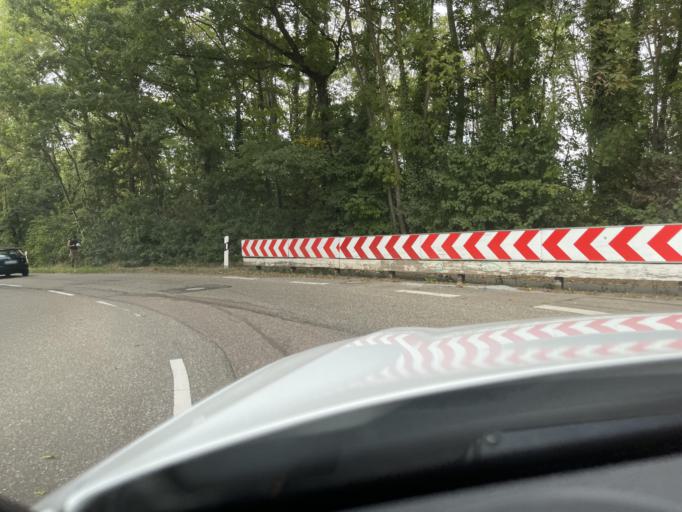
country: DE
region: Baden-Wuerttemberg
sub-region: Regierungsbezirk Stuttgart
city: Ludwigsburg
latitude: 48.9061
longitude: 9.2182
